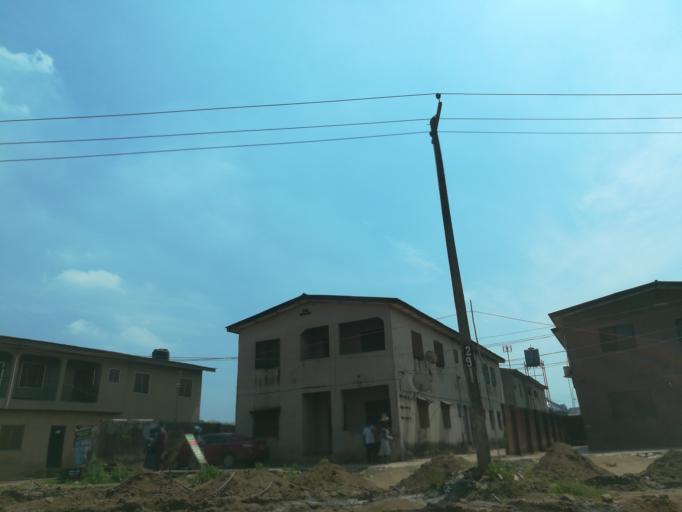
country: NG
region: Lagos
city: Ikorodu
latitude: 6.6498
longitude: 3.4767
